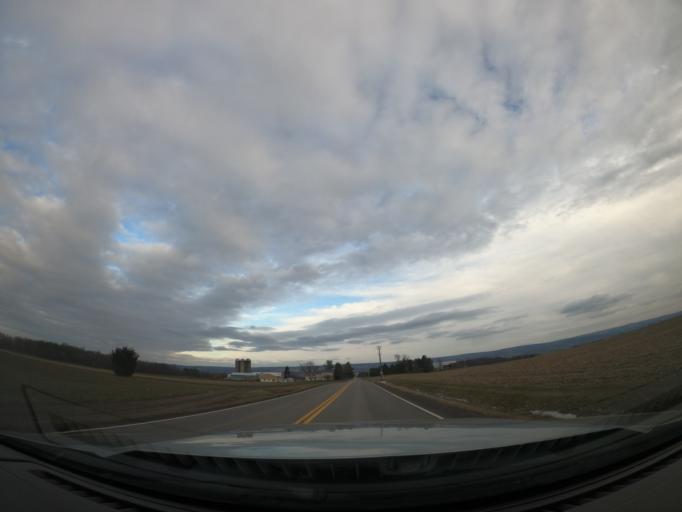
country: US
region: New York
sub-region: Yates County
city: Dundee
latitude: 42.4996
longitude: -76.9460
